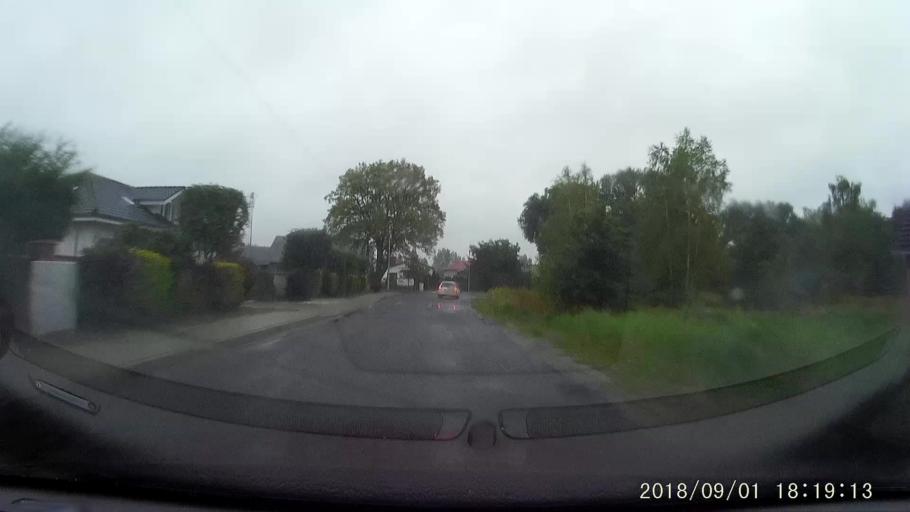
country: PL
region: Lower Silesian Voivodeship
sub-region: Powiat zgorzelecki
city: Piensk
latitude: 51.2558
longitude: 15.0460
